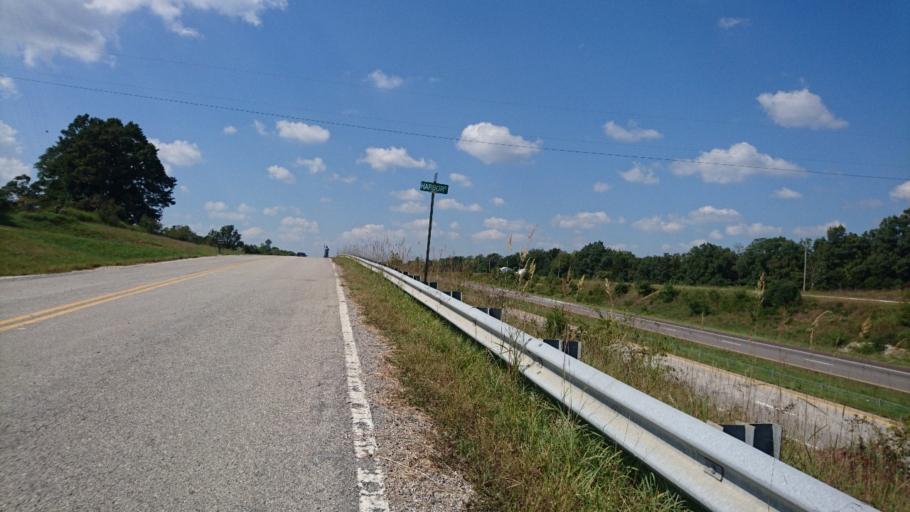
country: US
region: Missouri
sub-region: Pulaski County
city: Richland
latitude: 37.7568
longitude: -92.4764
